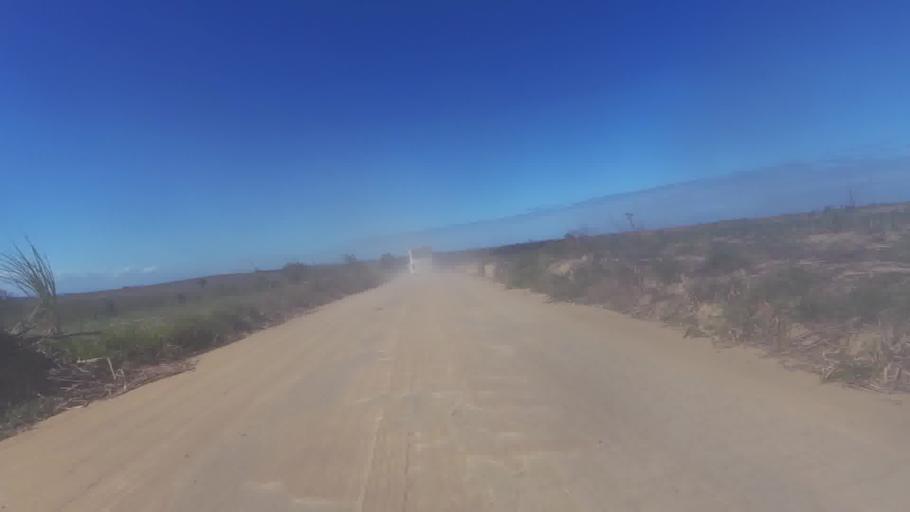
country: BR
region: Espirito Santo
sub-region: Marataizes
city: Marataizes
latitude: -21.1276
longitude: -40.9805
